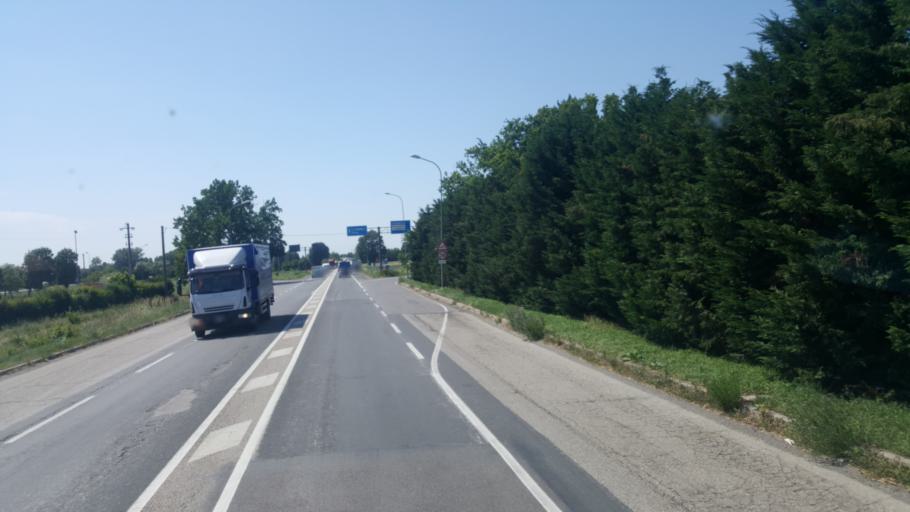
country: IT
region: Emilia-Romagna
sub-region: Provincia di Bologna
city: Castel Maggiore
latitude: 44.5938
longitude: 11.3829
